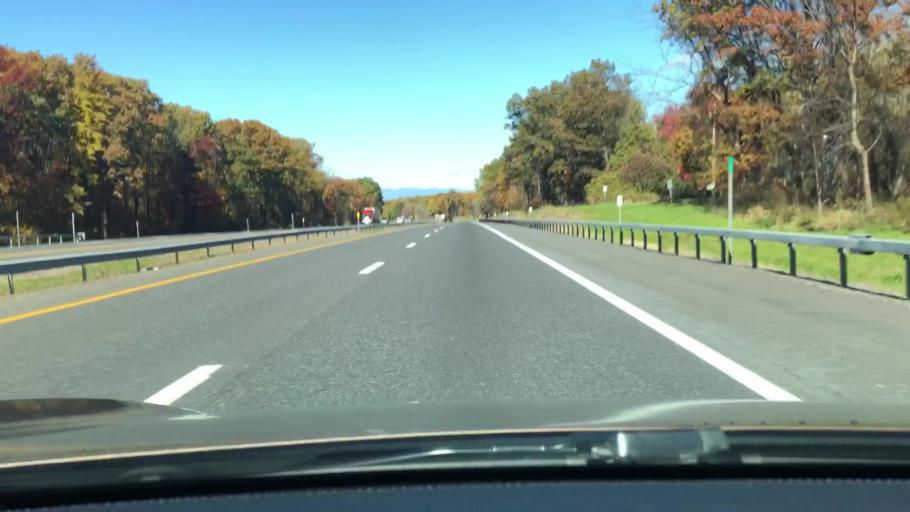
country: US
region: New York
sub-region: Ulster County
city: Clintondale
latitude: 41.6621
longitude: -74.0783
